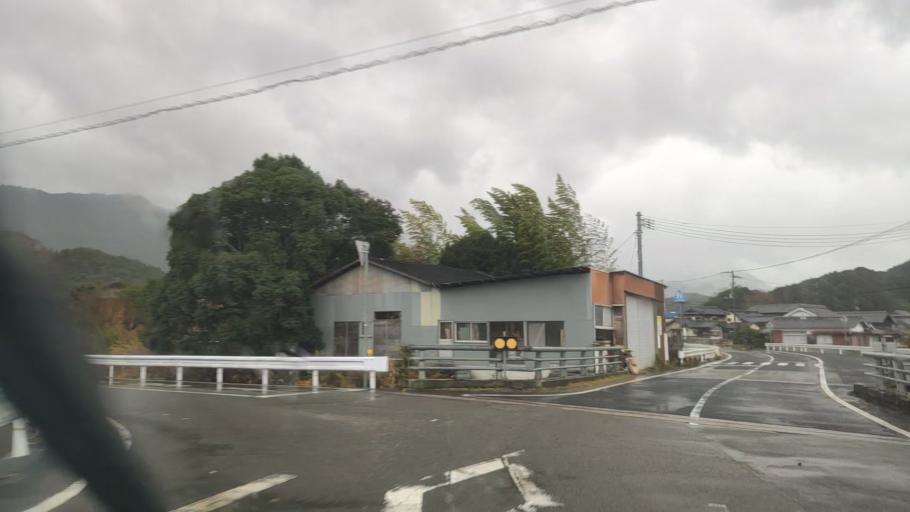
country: JP
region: Tokushima
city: Kamojimacho-jogejima
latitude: 34.2176
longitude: 134.3775
